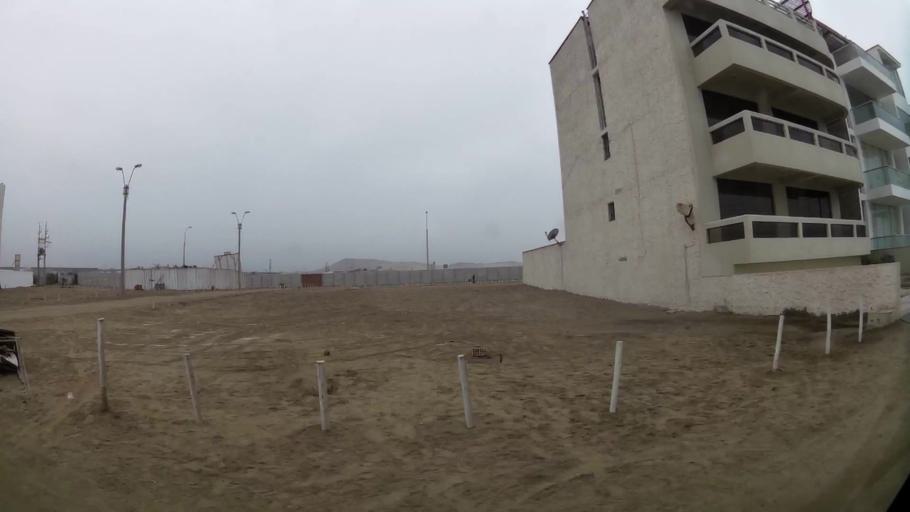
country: PE
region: Lima
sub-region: Lima
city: Punta Hermosa
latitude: -12.3264
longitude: -76.8339
